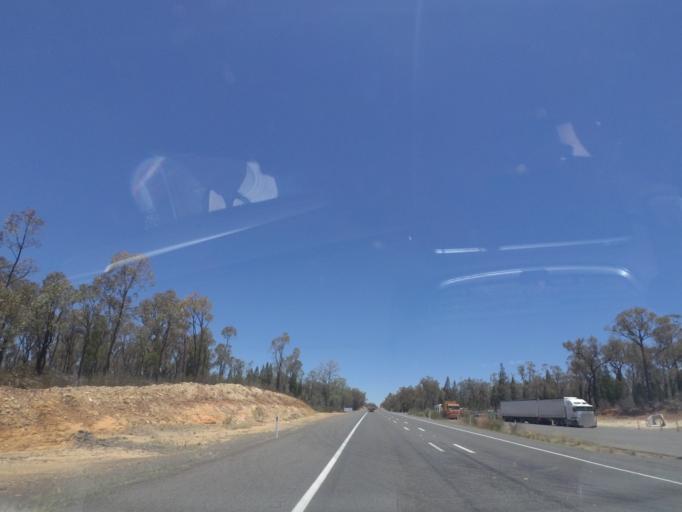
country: AU
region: New South Wales
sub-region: Warrumbungle Shire
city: Coonabarabran
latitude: -30.9184
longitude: 149.4335
